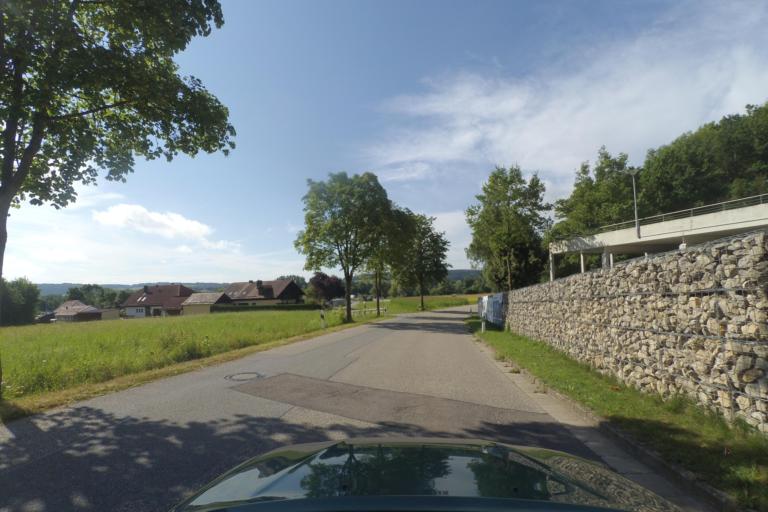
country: DE
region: Bavaria
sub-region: Lower Bavaria
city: Teugn
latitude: 48.9321
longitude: 11.9862
